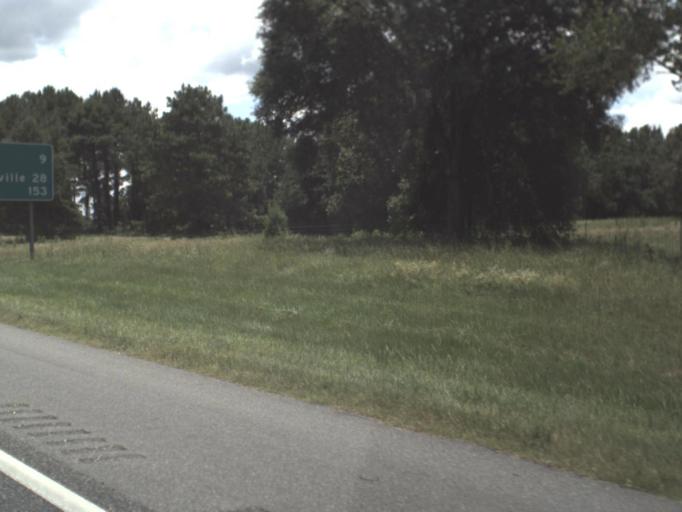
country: US
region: Florida
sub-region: Alachua County
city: High Springs
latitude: 29.9926
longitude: -82.5856
